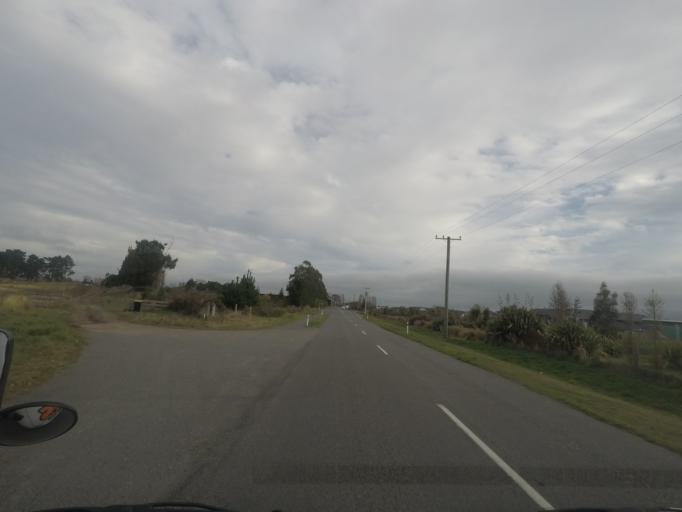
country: NZ
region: Canterbury
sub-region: Waimakariri District
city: Woodend
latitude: -43.2885
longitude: 172.7059
